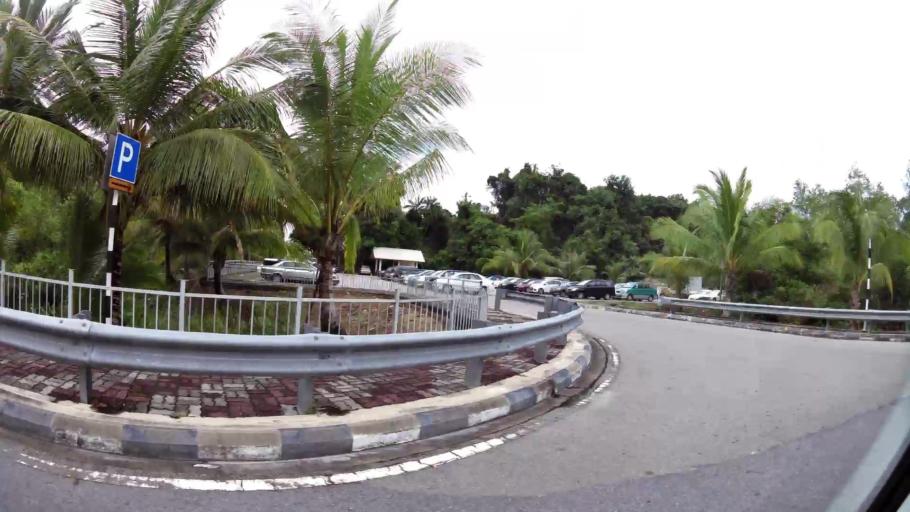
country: BN
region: Brunei and Muara
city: Bandar Seri Begawan
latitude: 4.8824
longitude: 114.9303
